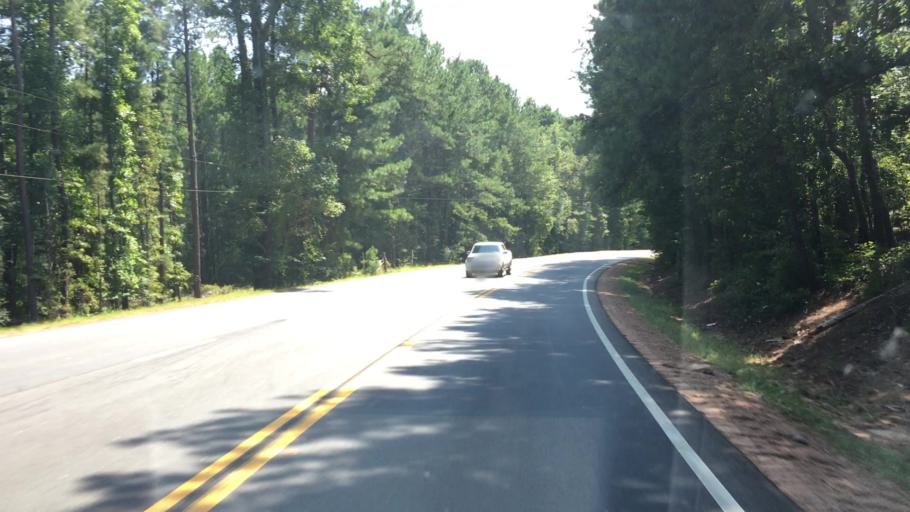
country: US
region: Georgia
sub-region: Oconee County
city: Watkinsville
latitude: 33.7276
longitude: -83.4307
